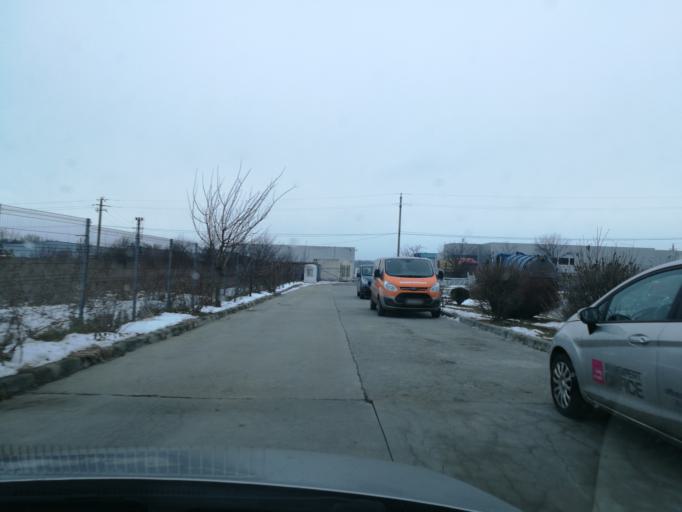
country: RO
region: Ilfov
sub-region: Comuna Tunari
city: Tunari
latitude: 44.5401
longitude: 26.1321
